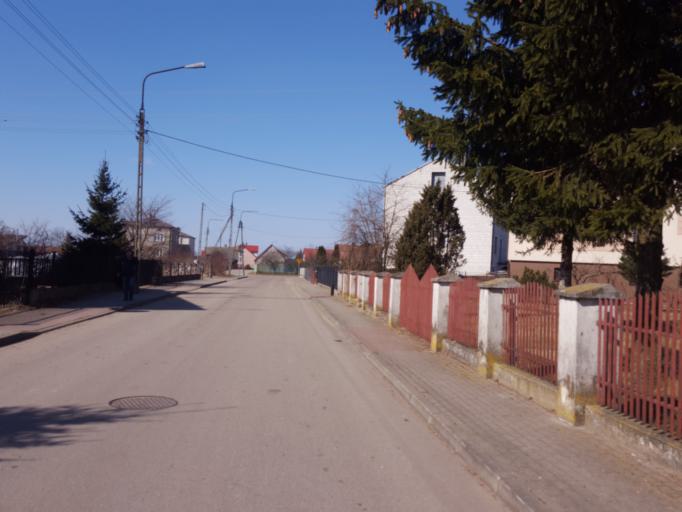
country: PL
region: Podlasie
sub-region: Powiat kolnenski
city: Stawiski
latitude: 53.3768
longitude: 22.1517
